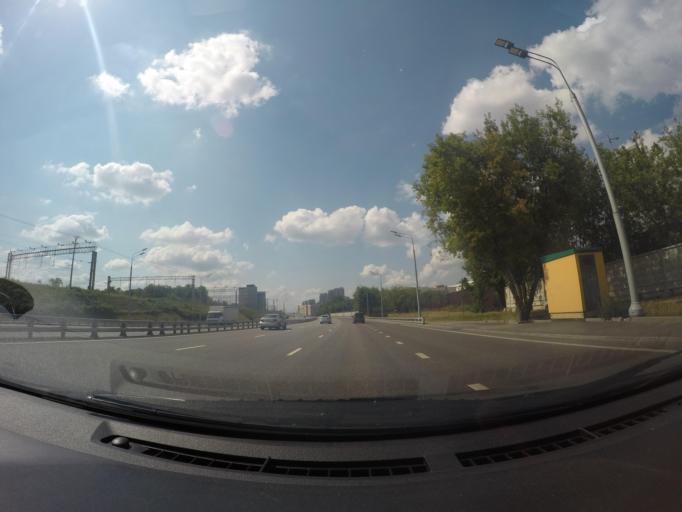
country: RU
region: Moscow
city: Leonovo
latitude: 55.8450
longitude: 37.6522
